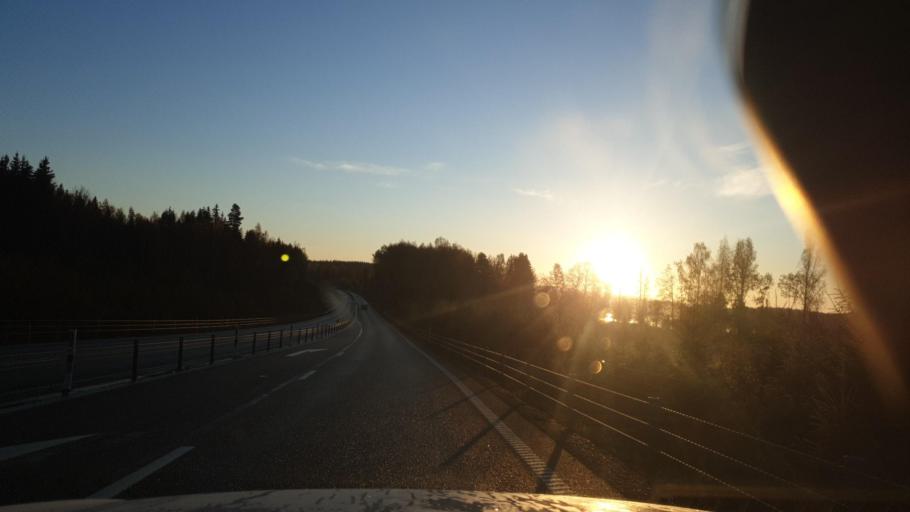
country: SE
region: Vaermland
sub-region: Eda Kommun
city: Amotfors
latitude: 59.7564
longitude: 12.4259
